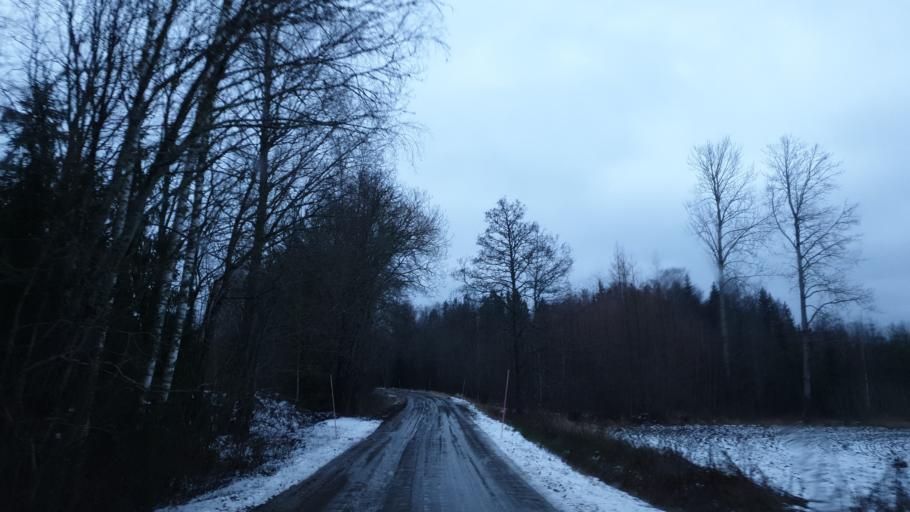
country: SE
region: Uppsala
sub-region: Tierps Kommun
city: Tierp
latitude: 60.3450
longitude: 17.4682
